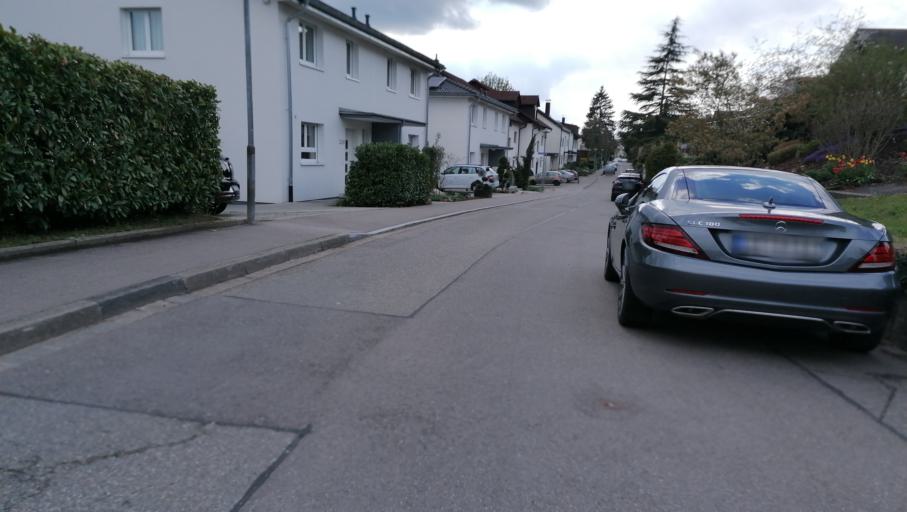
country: DE
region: Baden-Wuerttemberg
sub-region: Freiburg Region
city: Bad Sackingen
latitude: 47.5591
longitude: 7.9537
